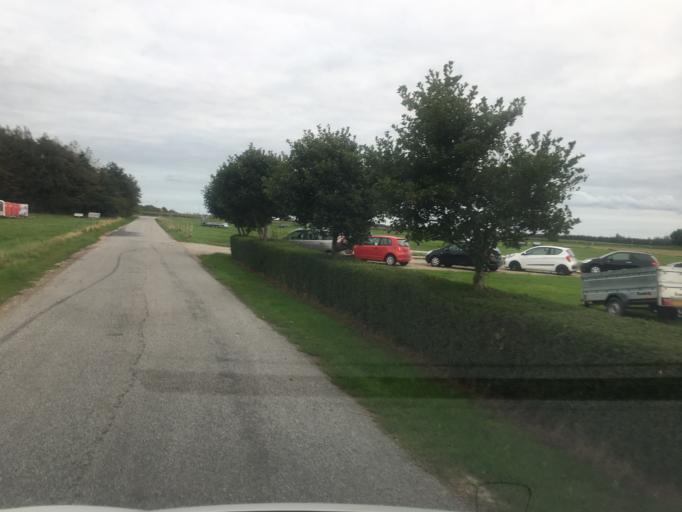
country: DK
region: South Denmark
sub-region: Tonder Kommune
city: Tonder
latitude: 54.9584
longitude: 8.9214
